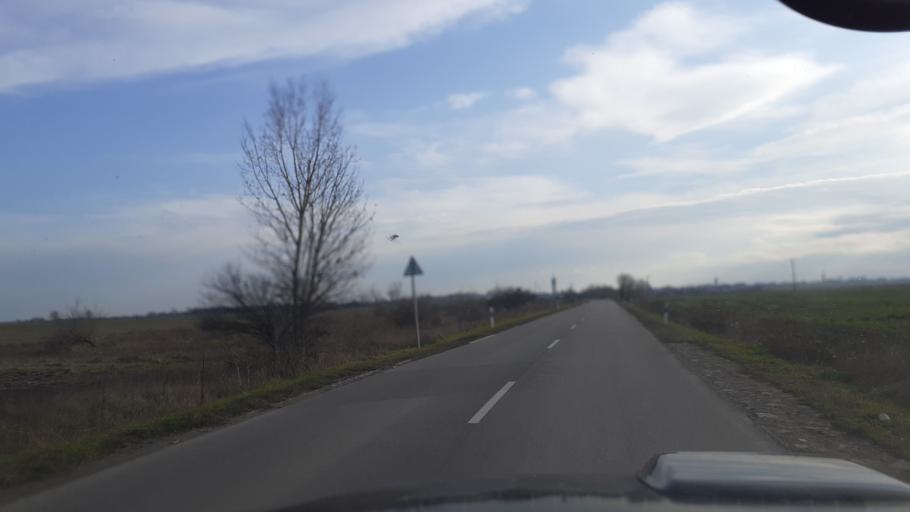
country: HU
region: Bacs-Kiskun
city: Kunszentmiklos
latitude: 47.0479
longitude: 19.1178
